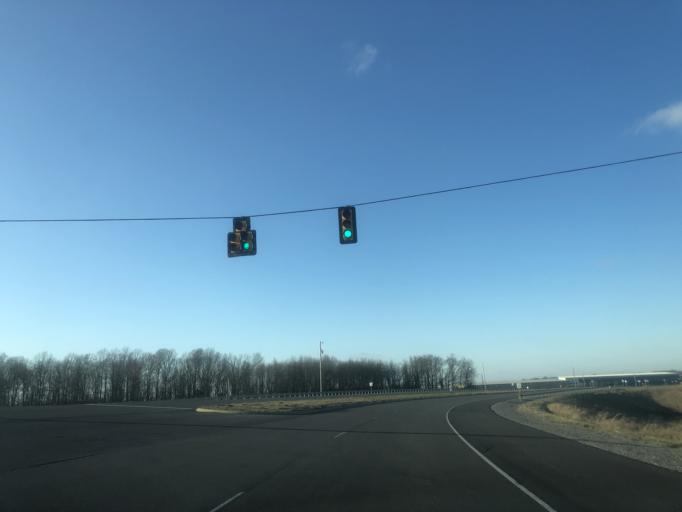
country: US
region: Tennessee
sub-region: Sumner County
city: Portland
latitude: 36.6322
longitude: -86.5753
